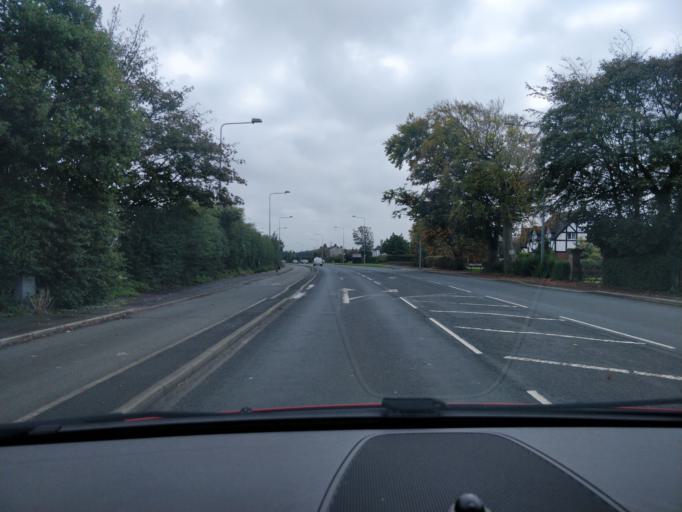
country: GB
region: England
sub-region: Sefton
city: Southport
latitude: 53.6251
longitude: -2.9624
